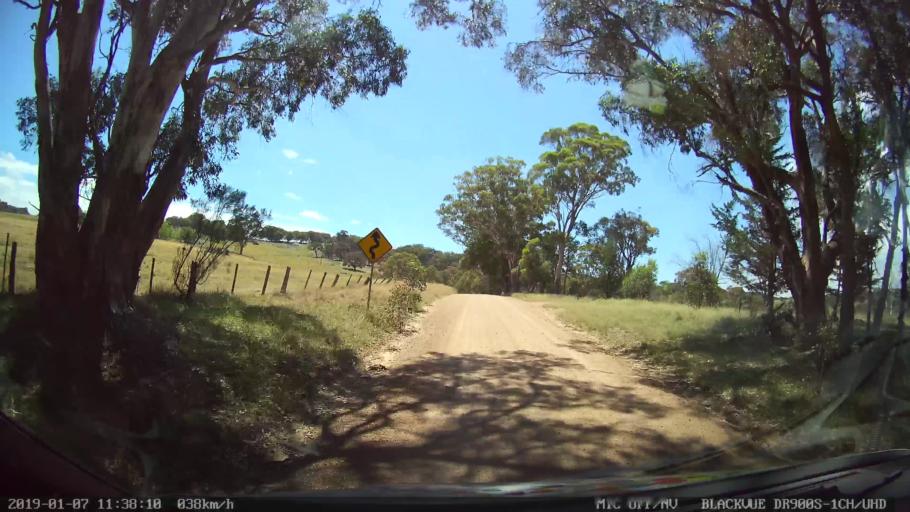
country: AU
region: New South Wales
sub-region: Armidale Dumaresq
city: Armidale
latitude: -30.3712
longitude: 151.5706
